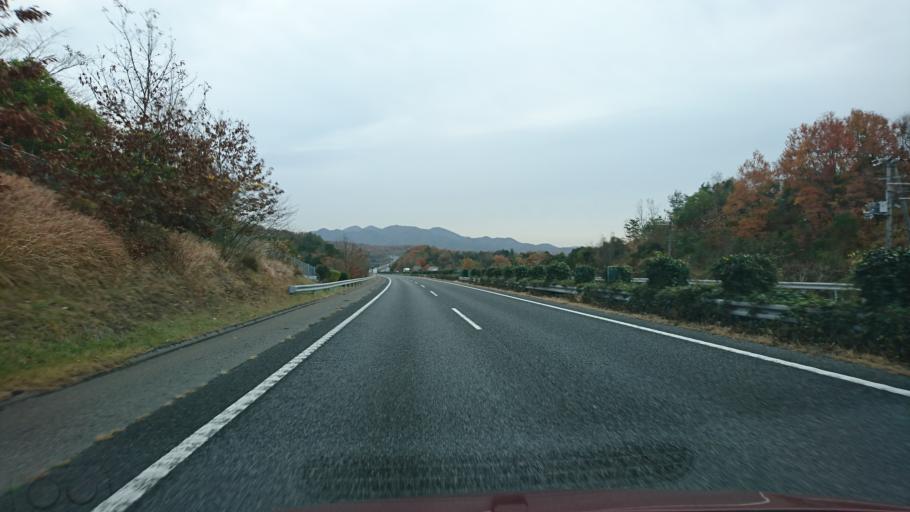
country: JP
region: Hyogo
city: Miki
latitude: 34.8030
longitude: 135.0363
